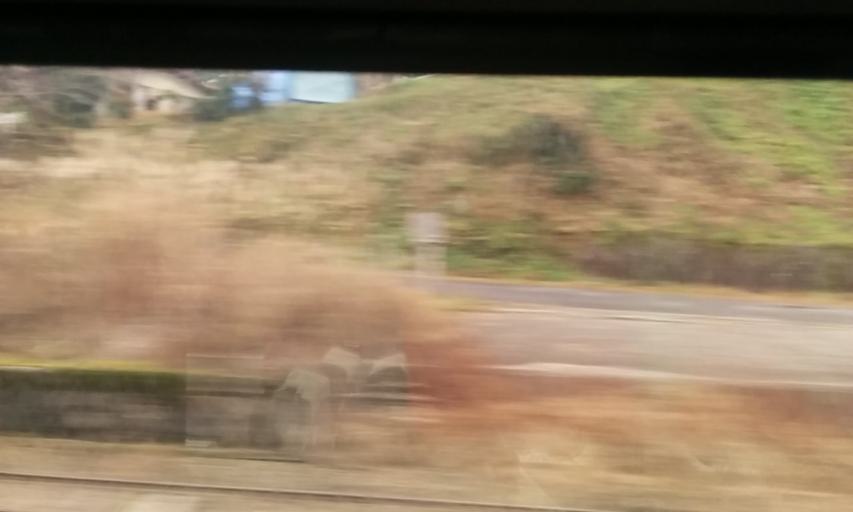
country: JP
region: Gifu
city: Nakatsugawa
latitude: 35.5260
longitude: 137.5300
